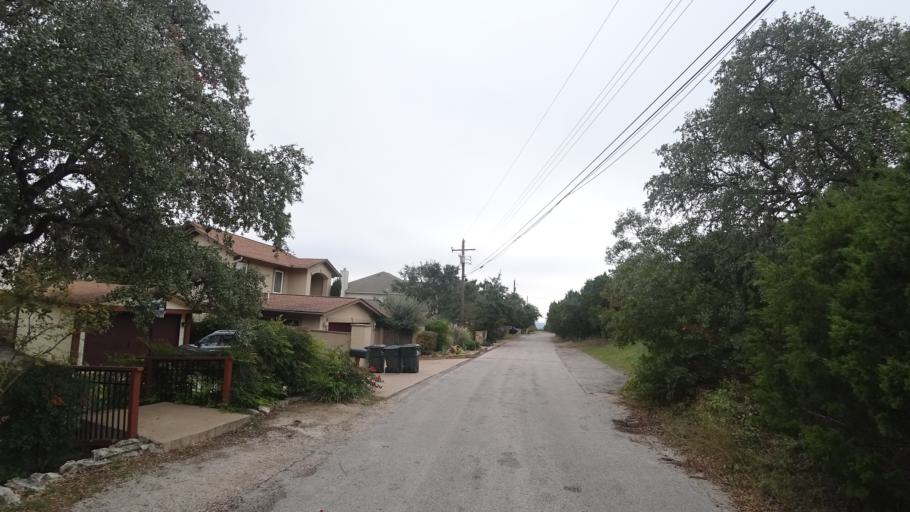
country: US
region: Texas
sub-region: Travis County
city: Hudson Bend
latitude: 30.3929
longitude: -97.9190
